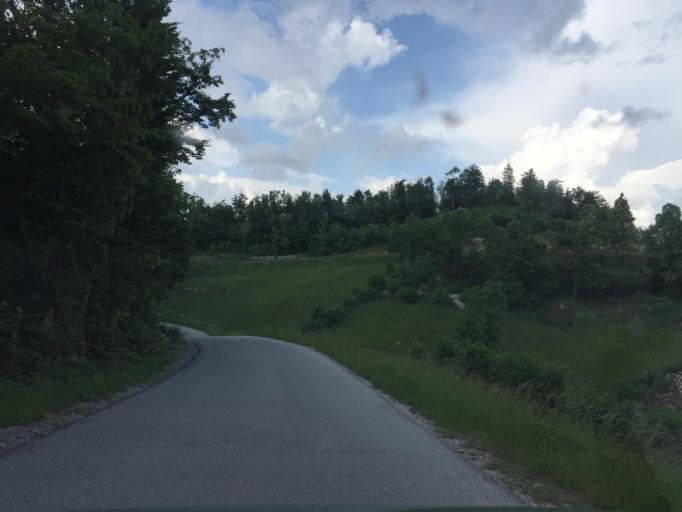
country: SI
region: Nova Gorica
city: Sempas
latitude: 46.0413
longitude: 13.7679
